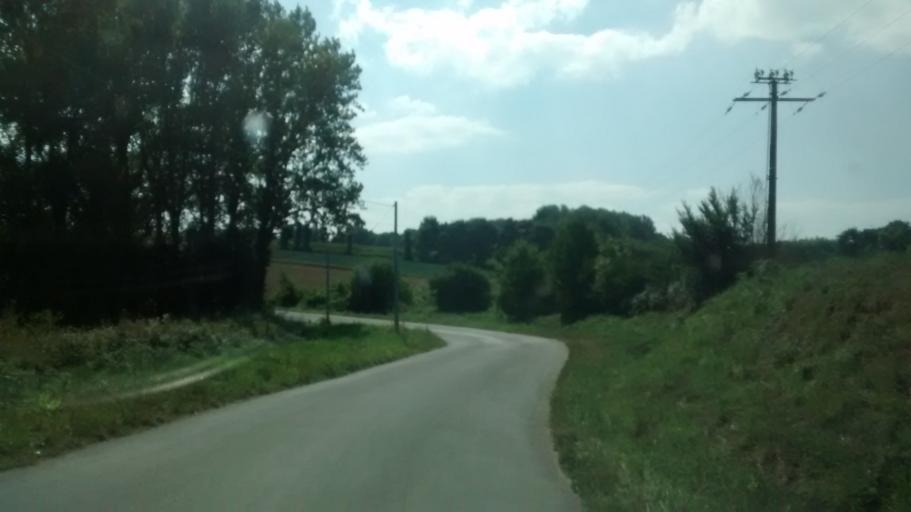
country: FR
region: Brittany
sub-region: Departement d'Ille-et-Vilaine
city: Saint-Coulomb
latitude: 48.6835
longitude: -1.8865
